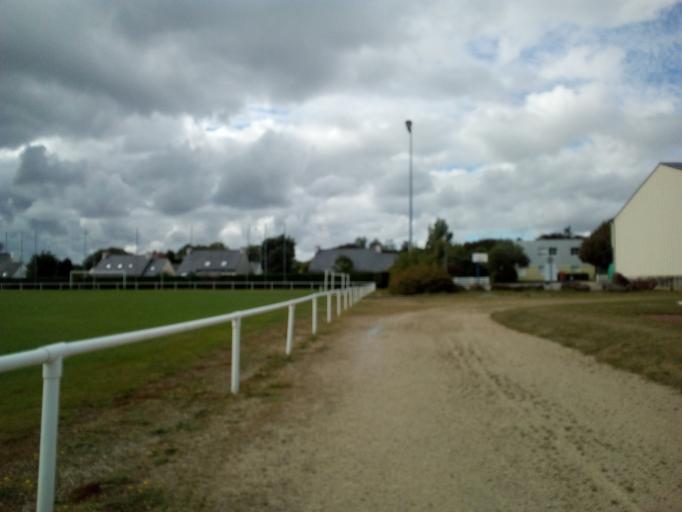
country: FR
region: Brittany
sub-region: Departement du Finistere
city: Landivisiau
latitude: 48.5134
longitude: -4.0650
